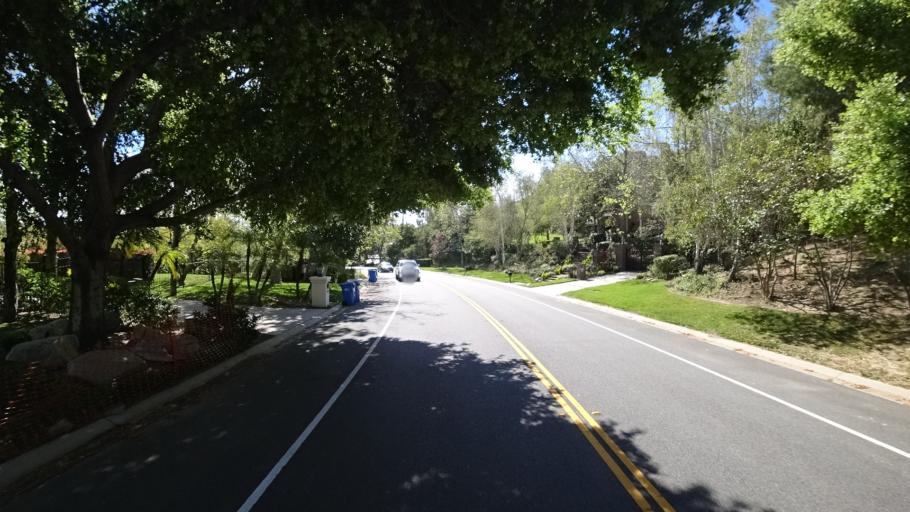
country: US
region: California
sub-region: Ventura County
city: Oak Park
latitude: 34.1874
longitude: -118.7997
